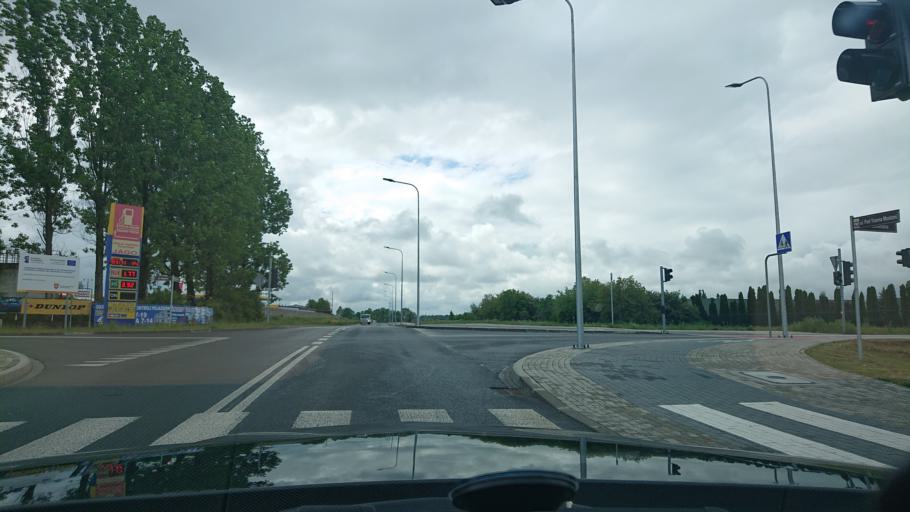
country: PL
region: Greater Poland Voivodeship
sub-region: Powiat gnieznienski
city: Gniezno
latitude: 52.5294
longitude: 17.6222
